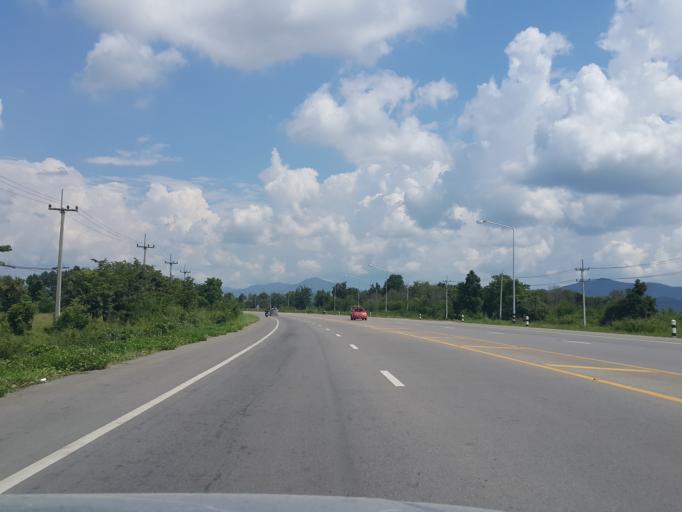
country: TH
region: Chiang Mai
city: San Kamphaeng
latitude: 18.7110
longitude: 99.1316
